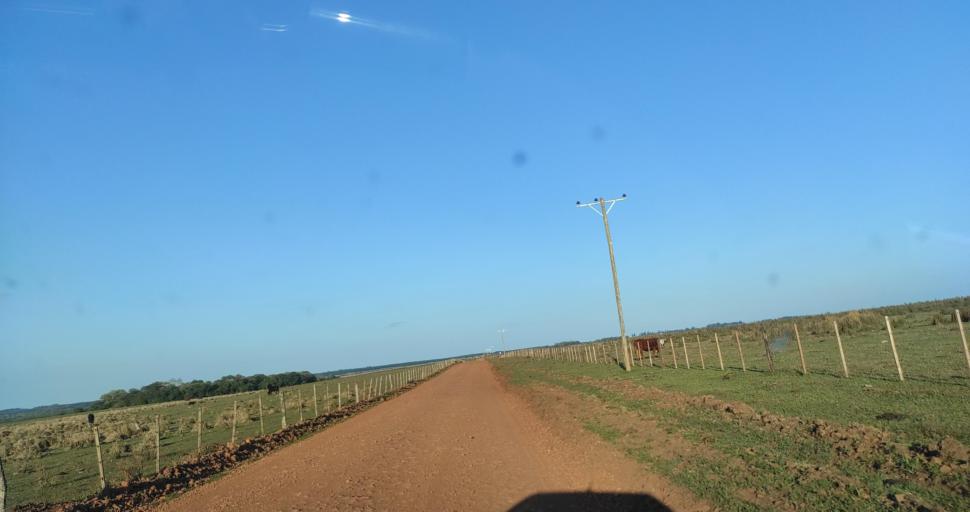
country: PY
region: Itapua
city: Carmen del Parana
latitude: -27.4088
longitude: -56.1598
